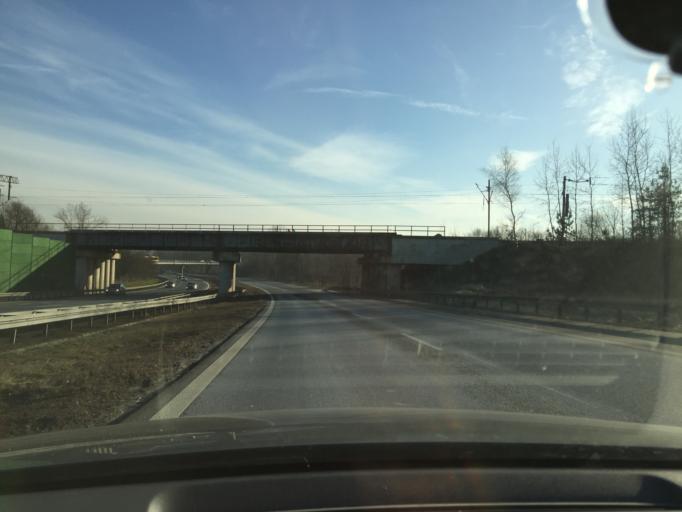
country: PL
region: Silesian Voivodeship
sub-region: Katowice
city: Murcki
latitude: 50.2325
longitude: 19.0642
